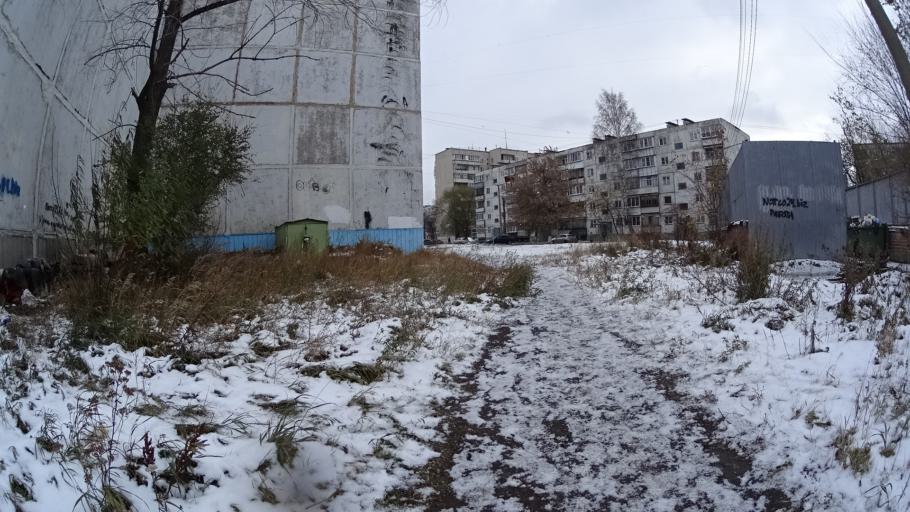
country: RU
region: Chelyabinsk
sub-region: Gorod Chelyabinsk
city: Chelyabinsk
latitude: 55.1903
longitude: 61.3109
